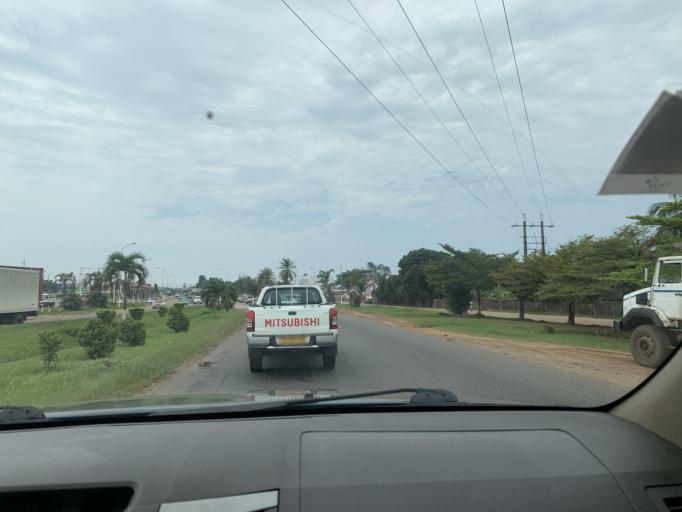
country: GA
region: Estuaire
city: Libreville
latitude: 0.3390
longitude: 9.4781
